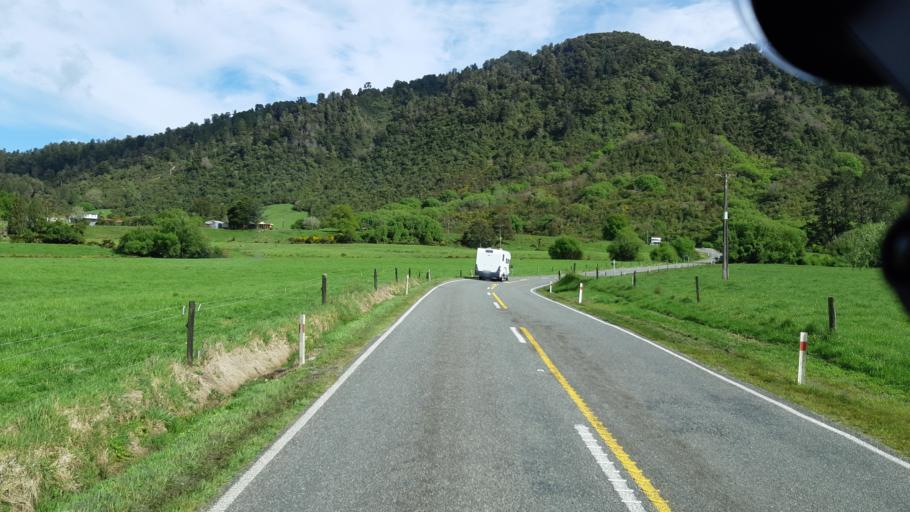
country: NZ
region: West Coast
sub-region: Buller District
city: Westport
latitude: -41.8606
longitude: 171.9407
